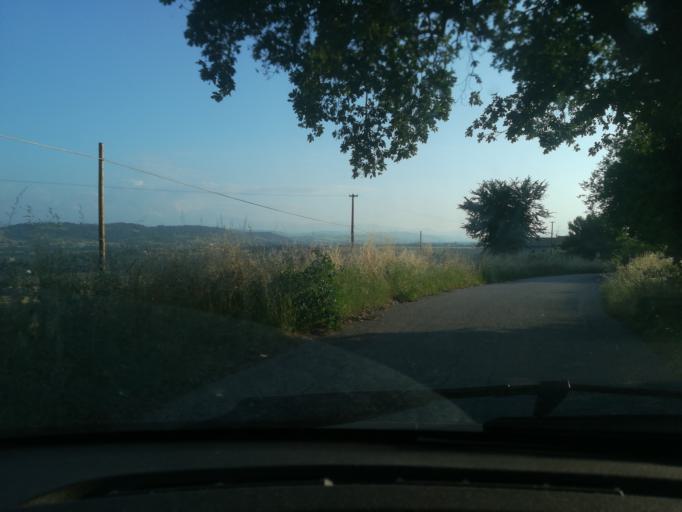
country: IT
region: The Marches
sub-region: Provincia di Macerata
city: Macerata
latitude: 43.2793
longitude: 13.4639
